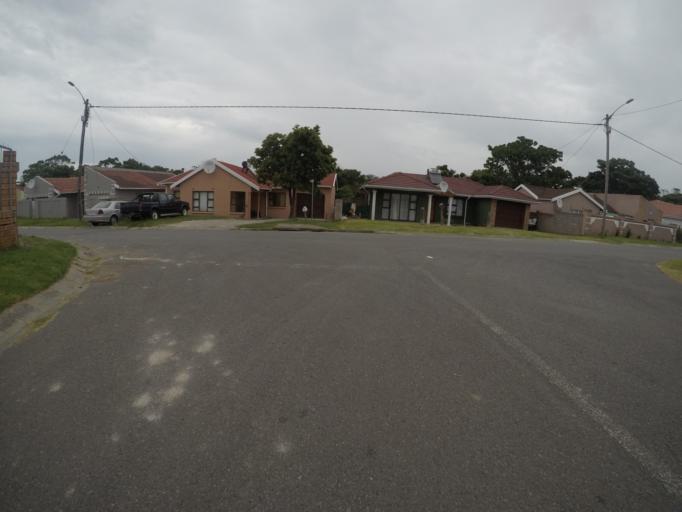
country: ZA
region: Eastern Cape
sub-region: Buffalo City Metropolitan Municipality
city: East London
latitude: -32.9966
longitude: 27.8458
